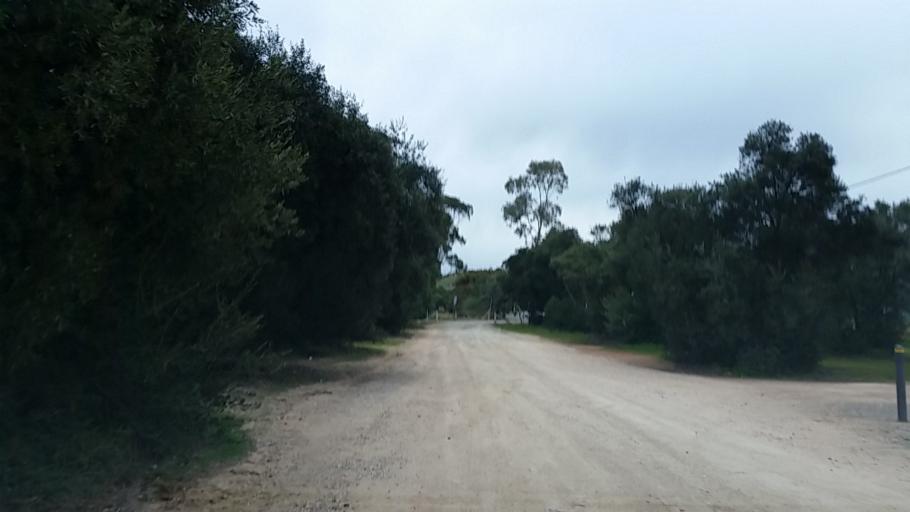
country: AU
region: South Australia
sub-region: Mid Murray
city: Mannum
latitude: -34.8547
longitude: 139.1623
